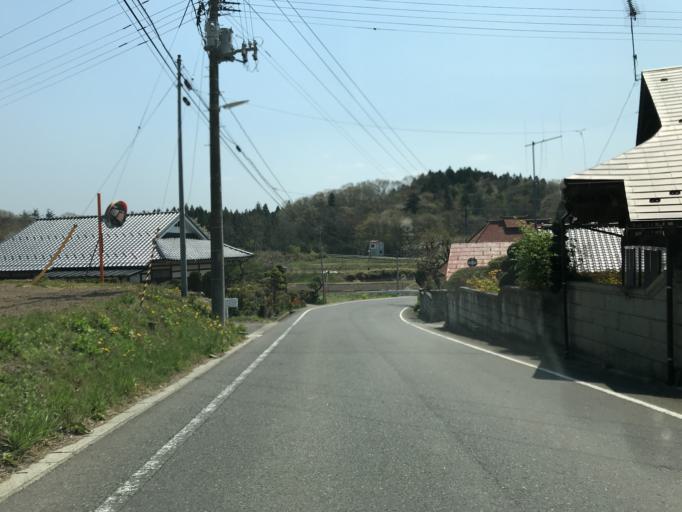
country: JP
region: Fukushima
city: Ishikawa
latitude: 37.1068
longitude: 140.4004
